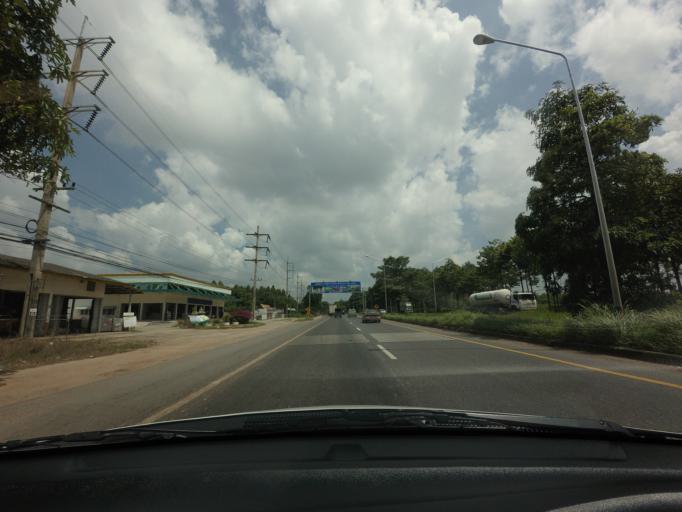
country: TH
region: Chachoengsao
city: Sanam Chai Khet
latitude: 13.7526
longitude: 101.4992
